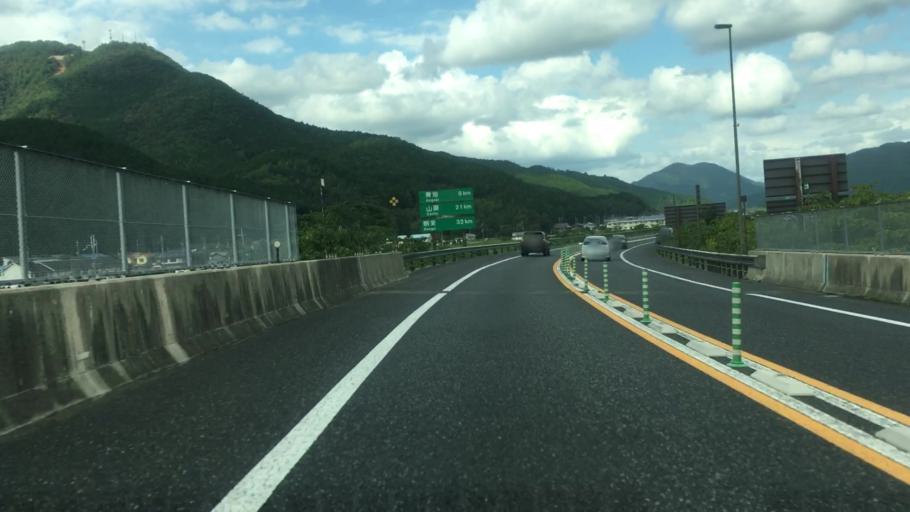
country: JP
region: Kyoto
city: Fukuchiyama
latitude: 35.1799
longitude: 135.0365
